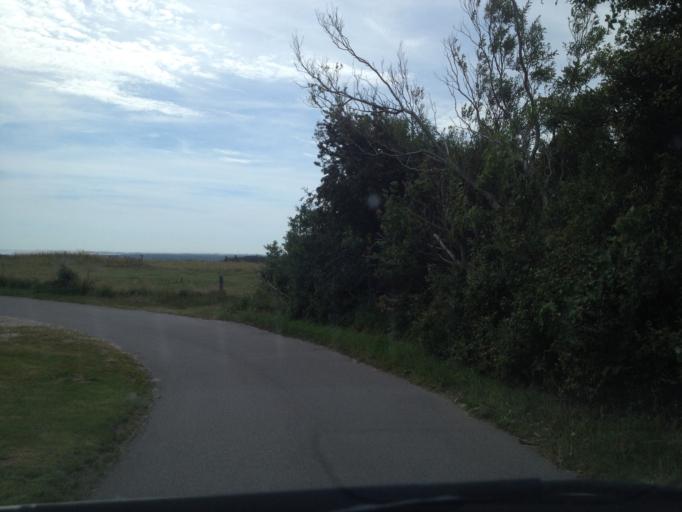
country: DK
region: Central Jutland
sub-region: Samso Kommune
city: Tranebjerg
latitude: 55.9690
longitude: 10.5274
